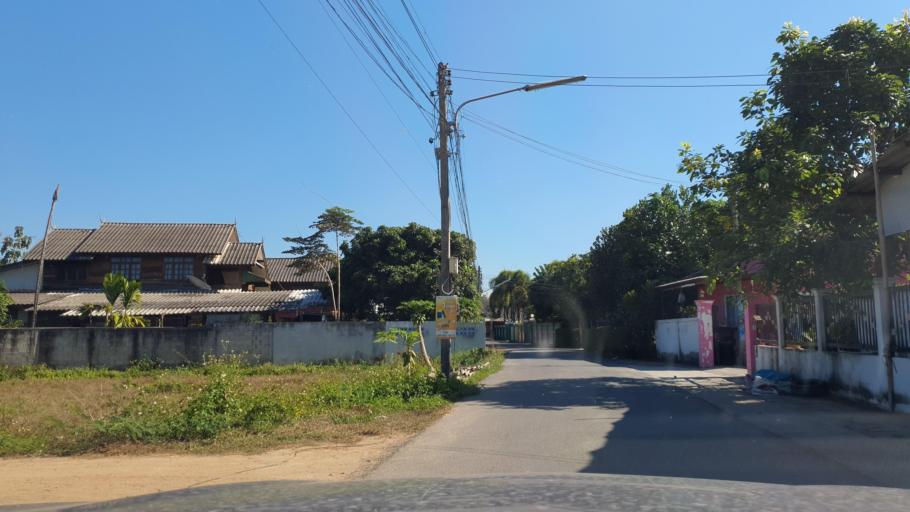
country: TH
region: Chiang Mai
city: San Pa Tong
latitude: 18.6403
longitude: 98.8796
